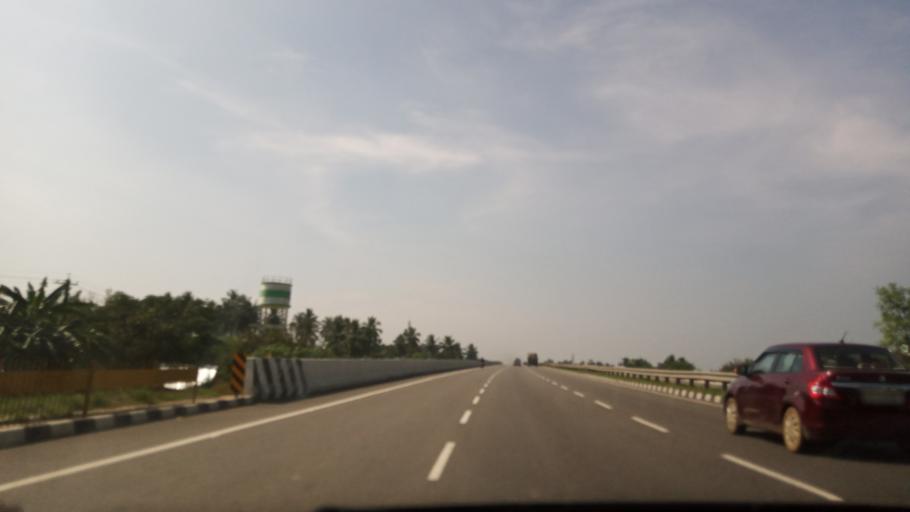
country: IN
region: Tamil Nadu
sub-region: Vellore
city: Pallikondai
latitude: 12.8889
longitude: 78.8992
